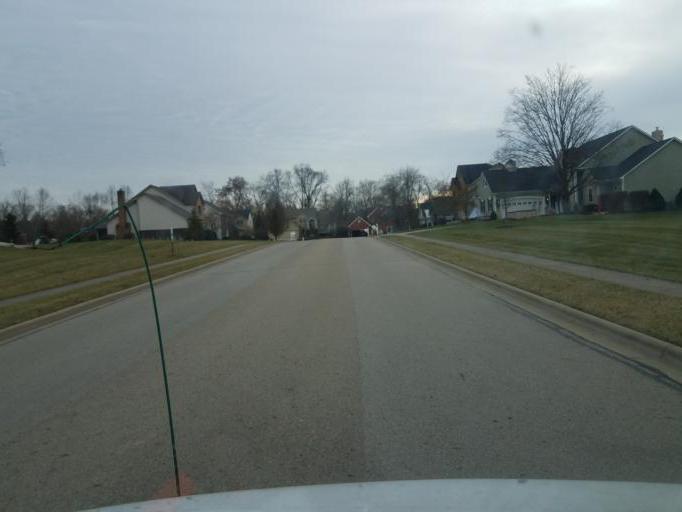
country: US
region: Ohio
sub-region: Franklin County
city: Westerville
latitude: 40.1747
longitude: -82.9419
